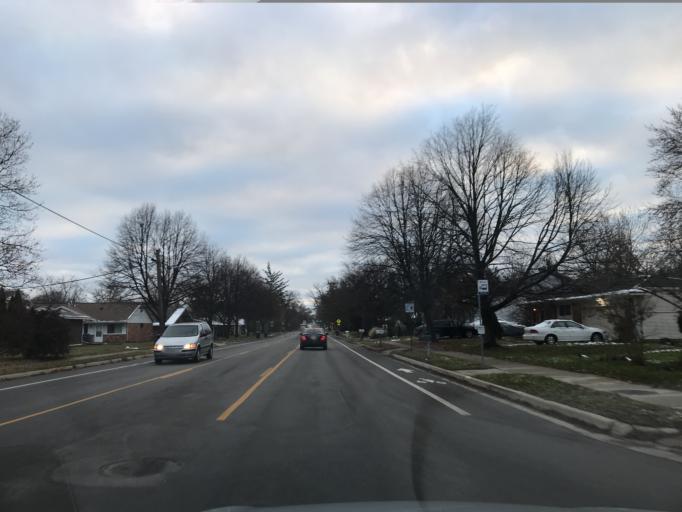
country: US
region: Michigan
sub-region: Washtenaw County
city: Ann Arbor
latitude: 42.2423
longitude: -83.7001
